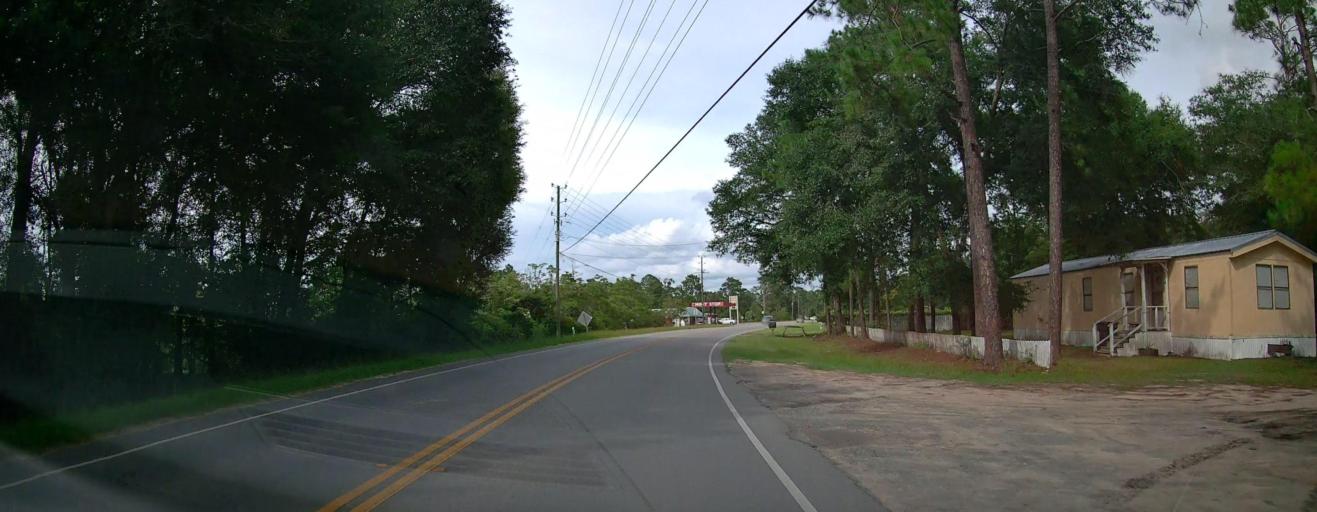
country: US
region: Georgia
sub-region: Wayne County
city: Jesup
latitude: 31.6617
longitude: -81.8874
